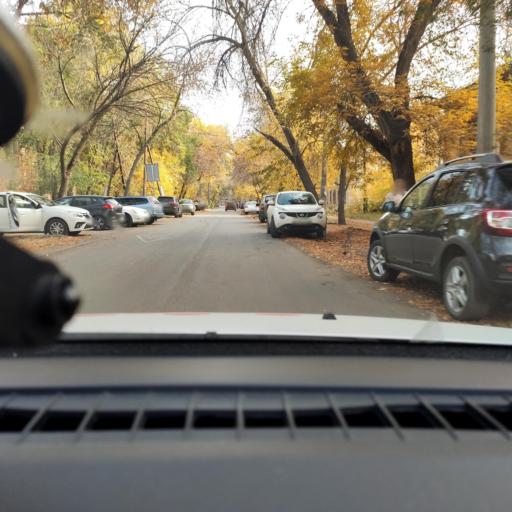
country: RU
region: Samara
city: Samara
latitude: 53.1183
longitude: 50.0787
